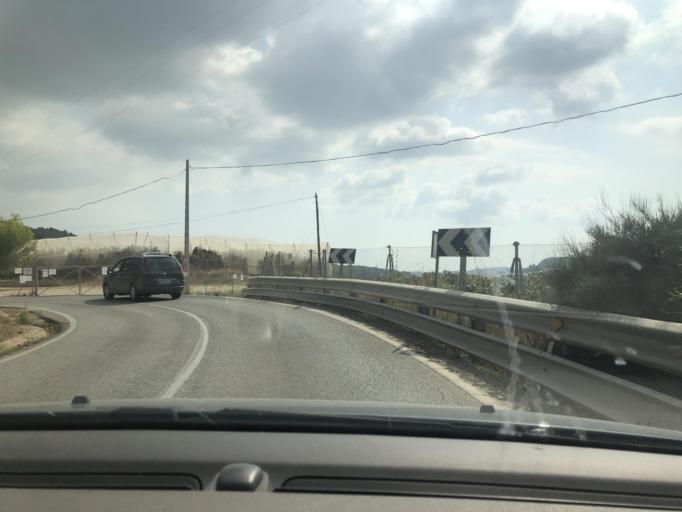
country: ES
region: Valencia
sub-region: Provincia de Alicante
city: Callosa d'En Sarria
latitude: 38.6552
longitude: -0.1030
